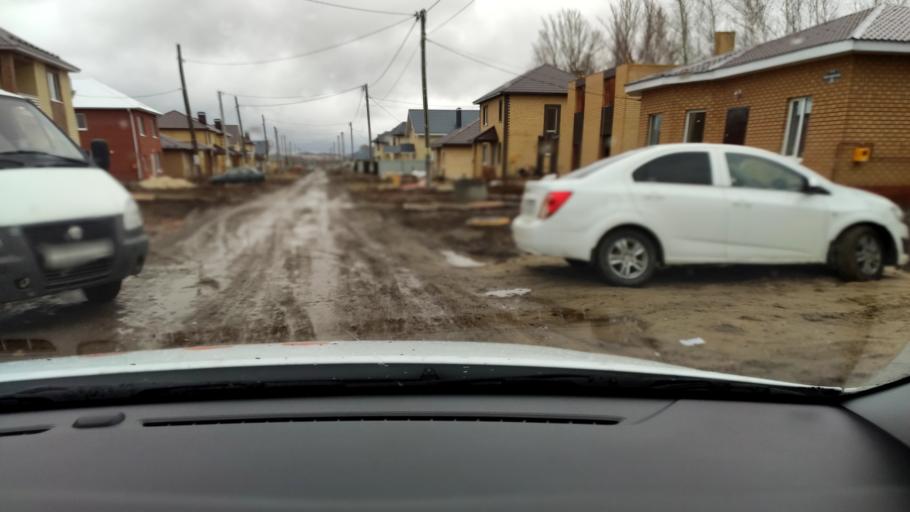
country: RU
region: Tatarstan
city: Stolbishchi
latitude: 55.7198
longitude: 49.3009
